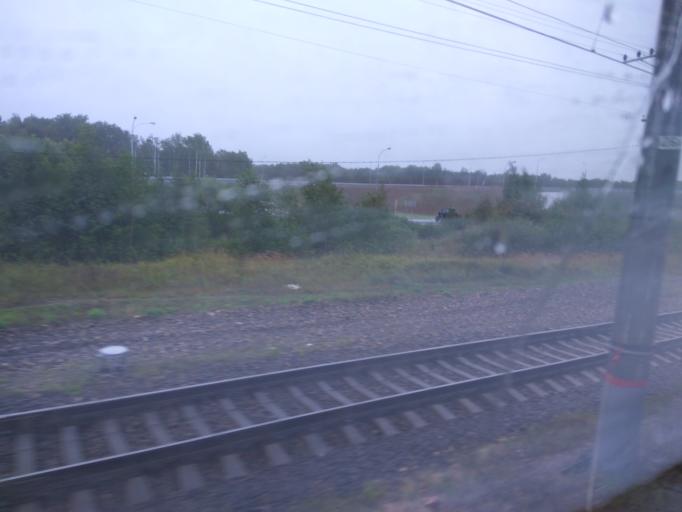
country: RU
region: Moskovskaya
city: Zhilevo
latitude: 54.9930
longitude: 38.0277
